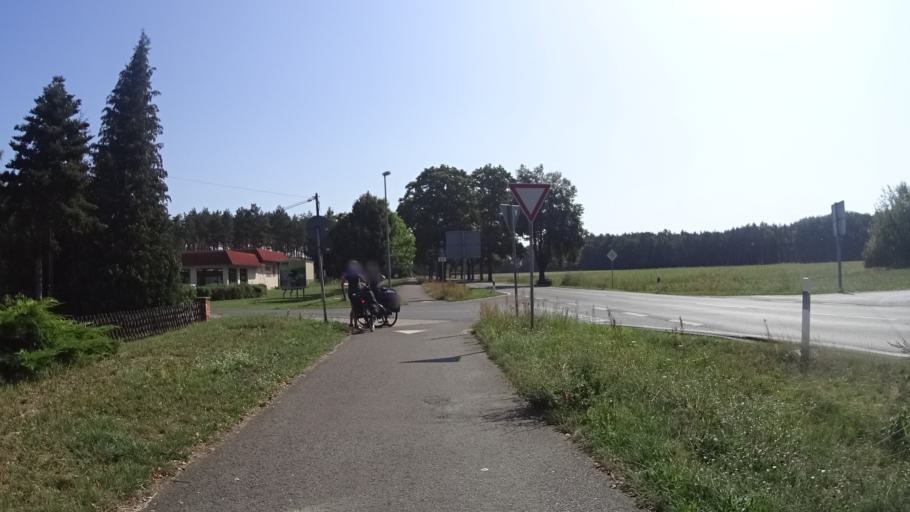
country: DE
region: Brandenburg
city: Guhrow
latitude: 51.8085
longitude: 14.2242
